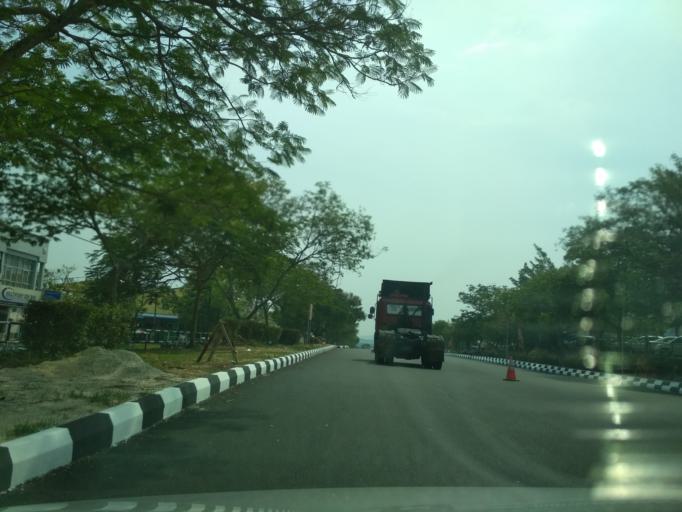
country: MY
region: Kedah
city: Kulim
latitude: 5.3700
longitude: 100.5653
